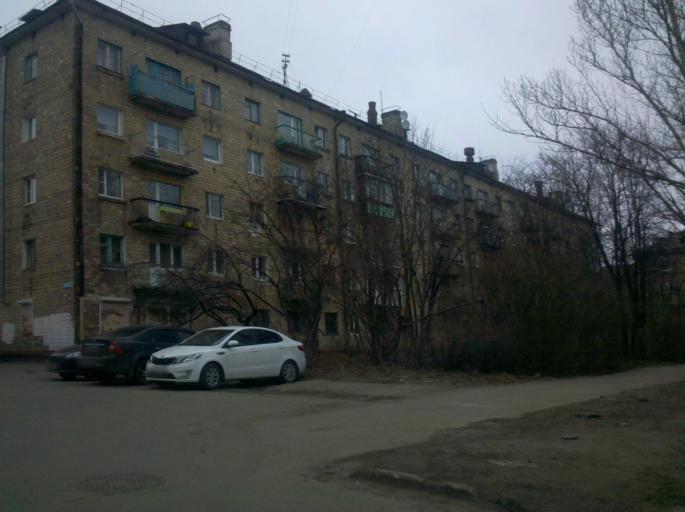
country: RU
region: Republic of Karelia
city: Petrozavodsk
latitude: 61.7842
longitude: 34.3542
